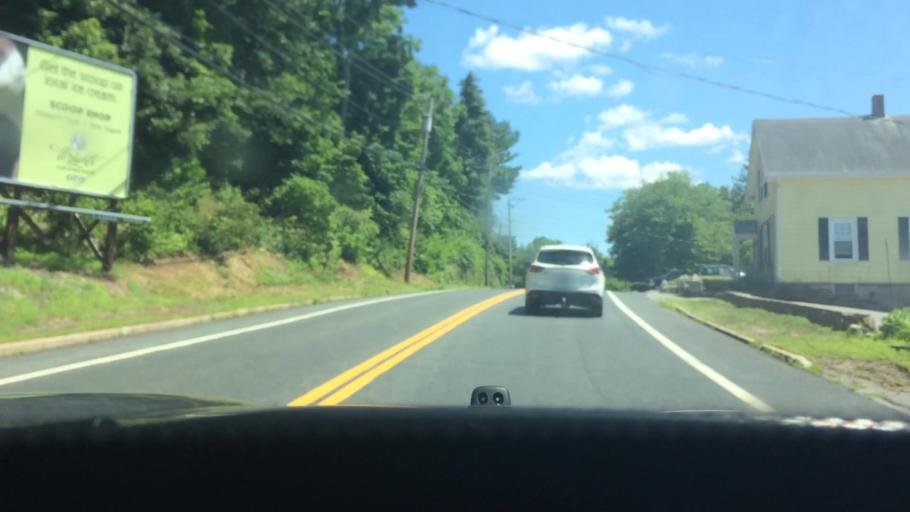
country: US
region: Massachusetts
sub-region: Worcester County
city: Blackstone
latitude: 41.9985
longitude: -71.5483
